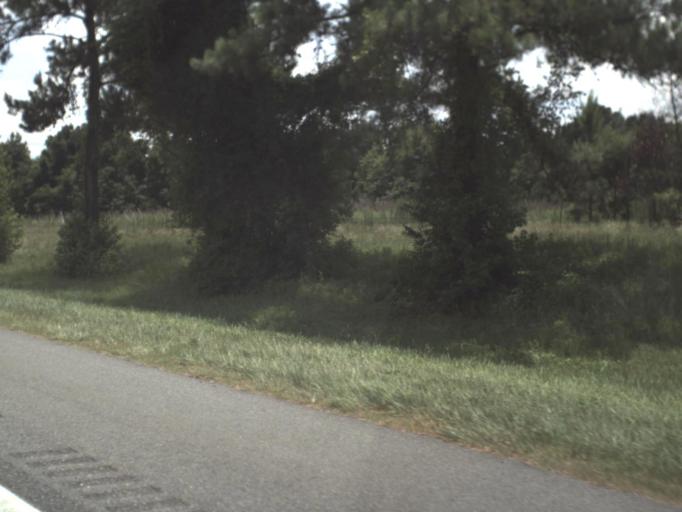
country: US
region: Florida
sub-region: Alachua County
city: High Springs
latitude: 29.9574
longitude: -82.5708
